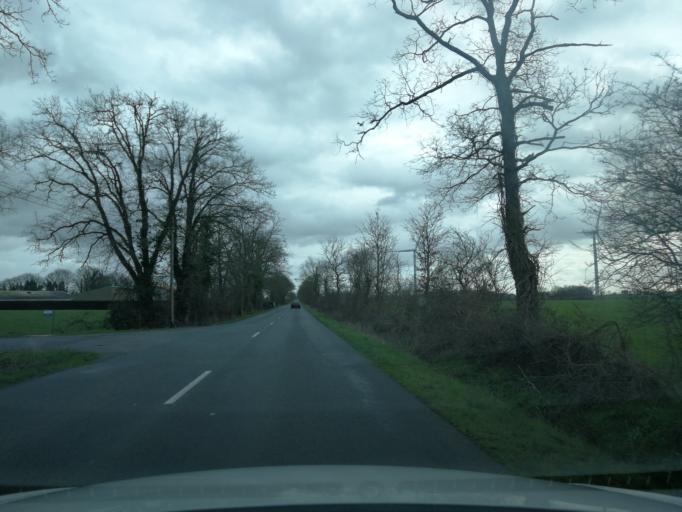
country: FR
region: Pays de la Loire
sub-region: Departement de la Loire-Atlantique
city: Montbert
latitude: 47.0152
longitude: -1.4832
